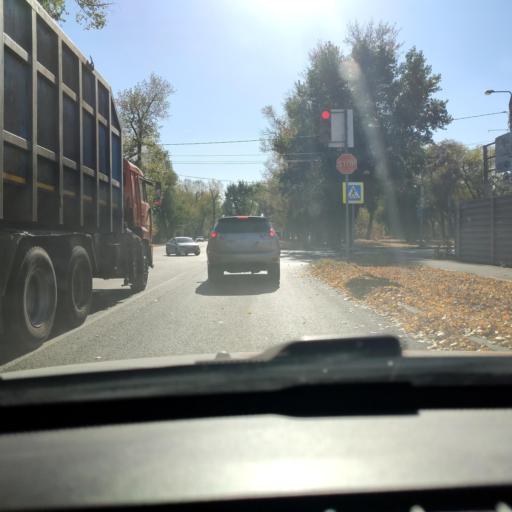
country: RU
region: Voronezj
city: Voronezh
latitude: 51.6645
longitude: 39.2524
